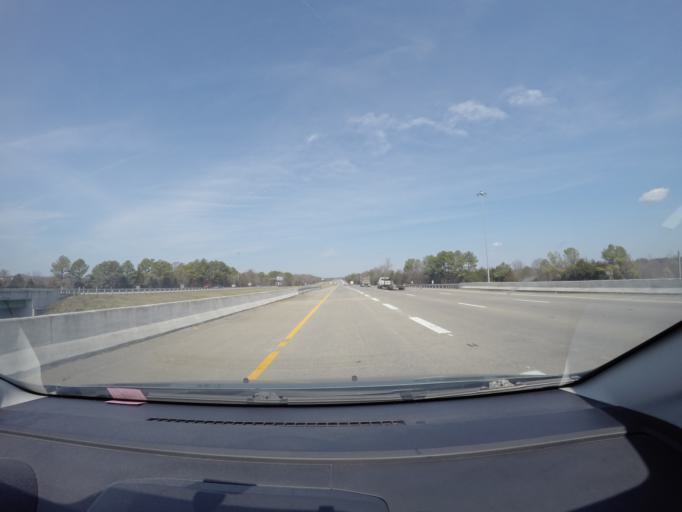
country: US
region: Tennessee
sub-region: Rutherford County
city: Smyrna
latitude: 35.9351
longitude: -86.5322
